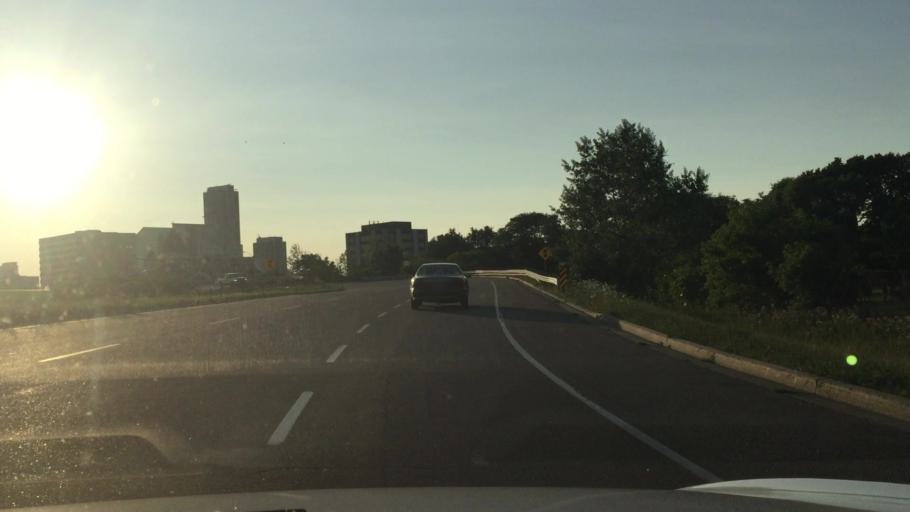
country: CA
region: Ontario
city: Scarborough
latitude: 43.7690
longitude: -79.3179
